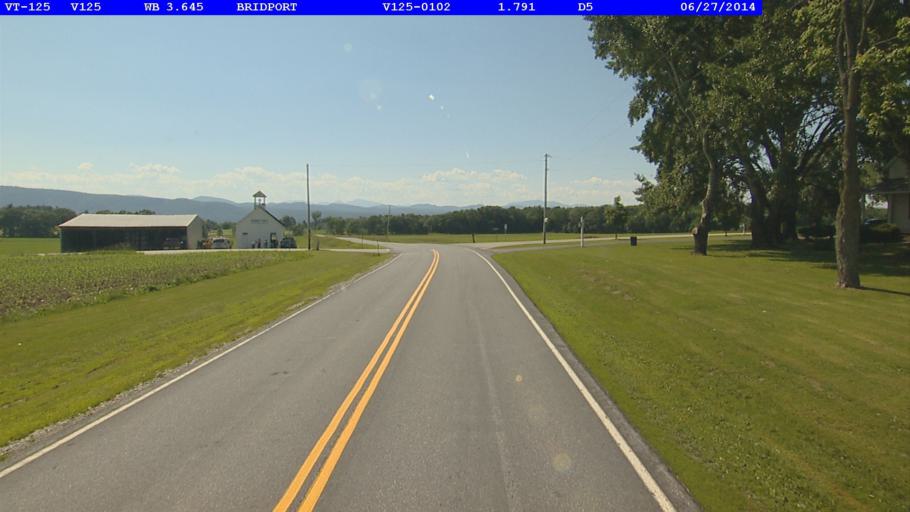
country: US
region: New York
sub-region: Essex County
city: Port Henry
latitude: 44.0039
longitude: -73.3725
